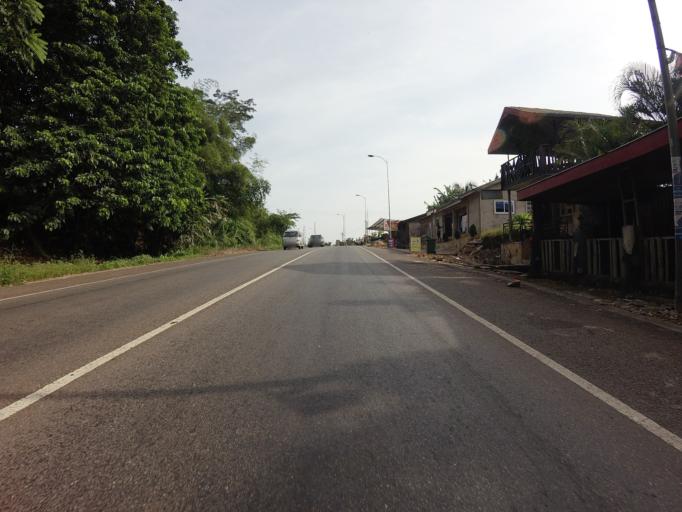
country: GH
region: Eastern
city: Aburi
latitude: 5.8535
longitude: -0.1703
